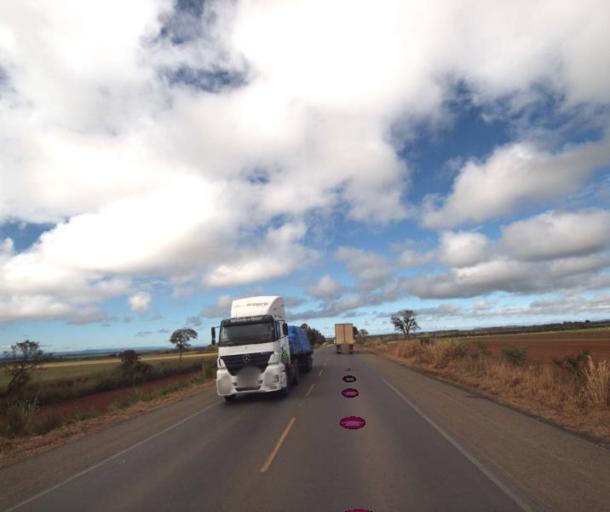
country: BR
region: Goias
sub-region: Uruacu
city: Uruacu
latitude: -14.7688
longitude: -49.2649
